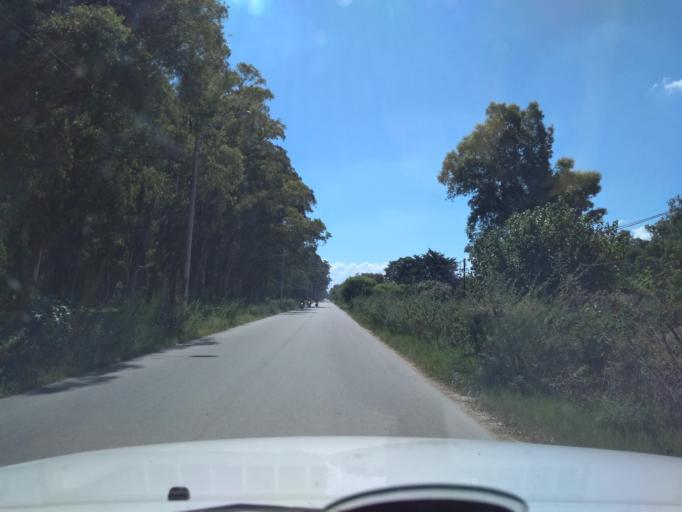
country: UY
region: Canelones
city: Barra de Carrasco
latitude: -34.8563
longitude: -56.0175
